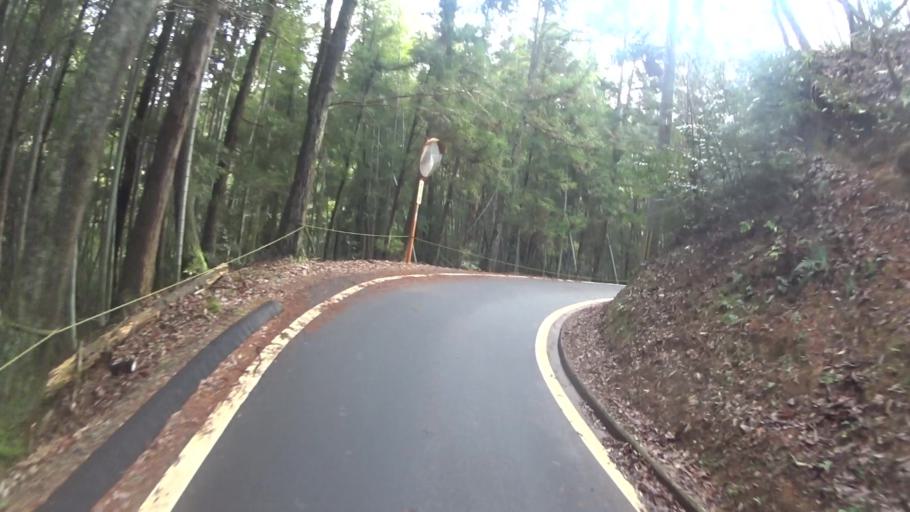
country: JP
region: Kyoto
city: Maizuru
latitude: 35.4381
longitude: 135.2989
